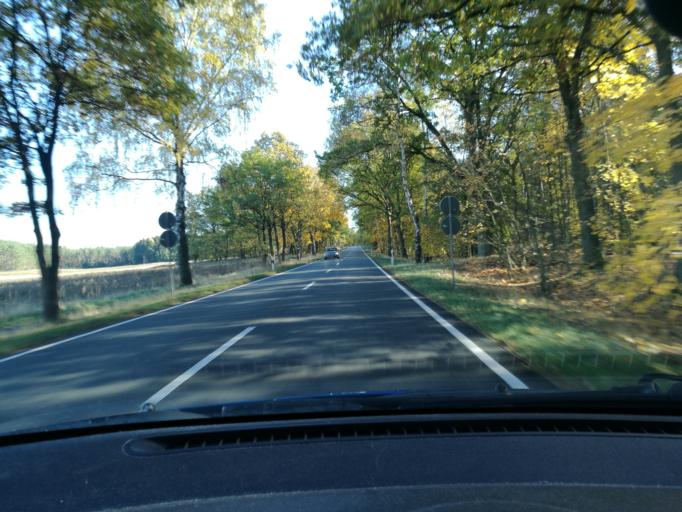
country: DE
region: Lower Saxony
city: Gohrde
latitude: 53.1498
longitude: 10.8505
